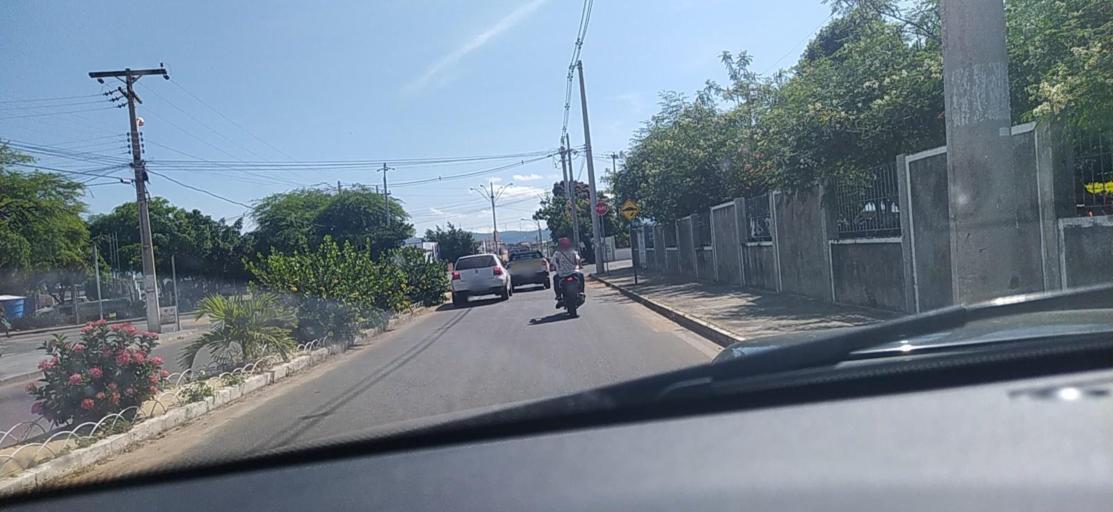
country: BR
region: Bahia
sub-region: Guanambi
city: Guanambi
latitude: -14.2131
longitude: -42.7650
